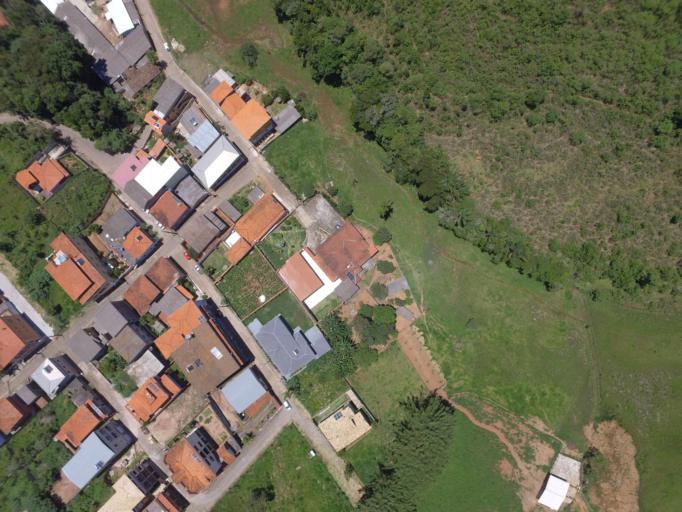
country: BR
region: Minas Gerais
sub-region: Tiradentes
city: Tiradentes
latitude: -21.0622
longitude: -44.0769
